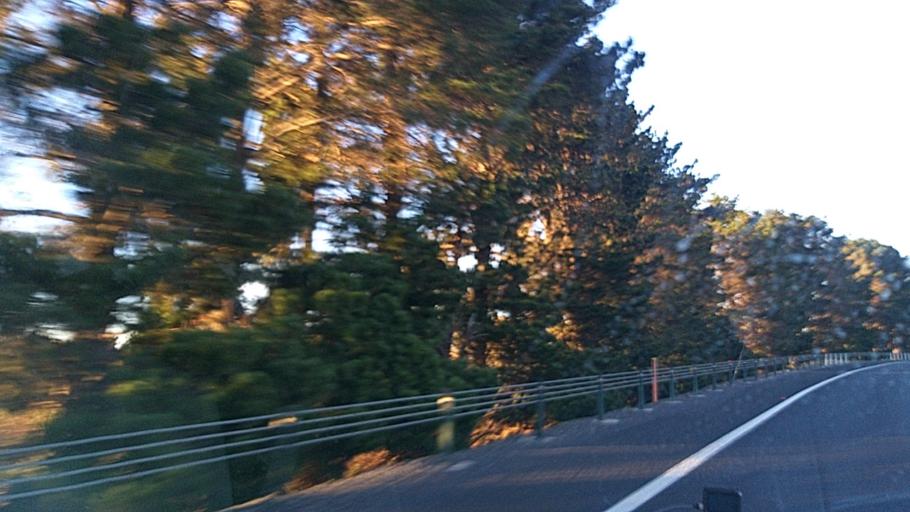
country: AU
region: New South Wales
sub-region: Goulburn Mulwaree
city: Goulburn
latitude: -34.8901
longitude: 149.5281
